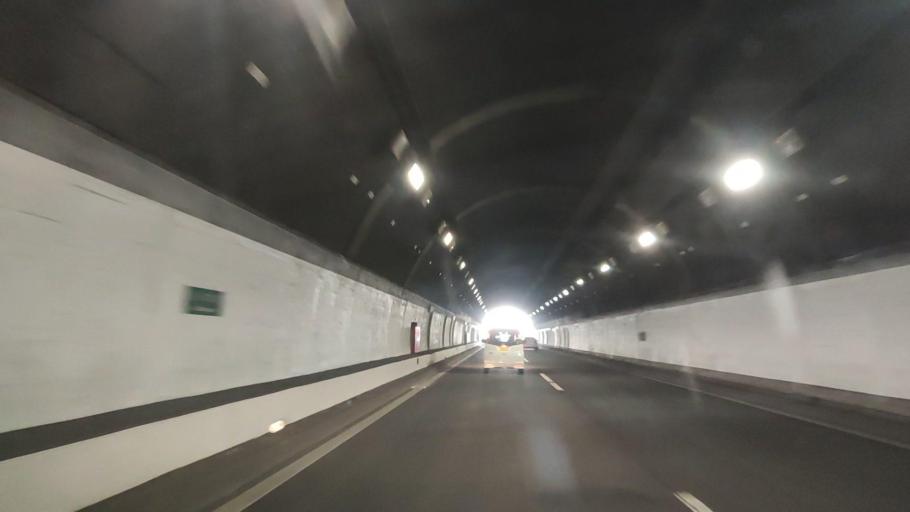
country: JP
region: Hyogo
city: Himeji
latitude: 34.8199
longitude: 134.6432
